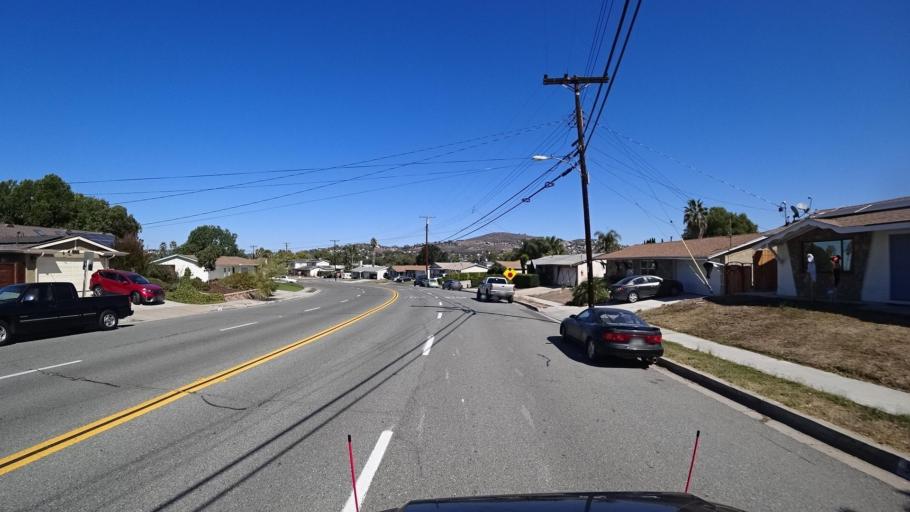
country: US
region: California
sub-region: San Diego County
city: La Presa
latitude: 32.7048
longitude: -117.0138
